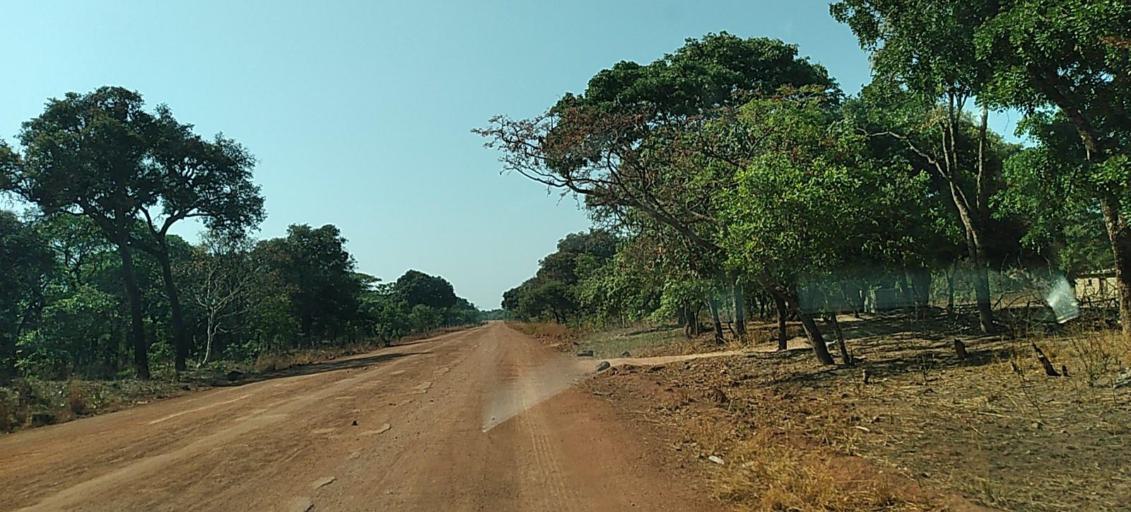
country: ZM
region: North-Western
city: Mwinilunga
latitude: -11.9245
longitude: 25.3198
